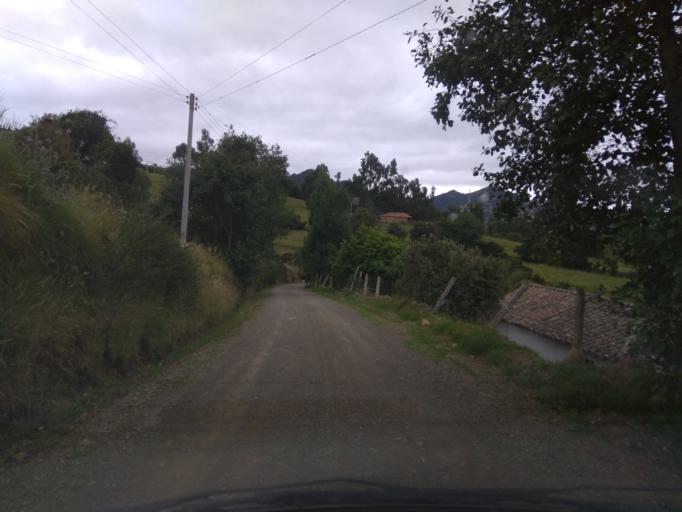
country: CO
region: Boyaca
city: Mongui
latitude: 5.7268
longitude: -72.8422
